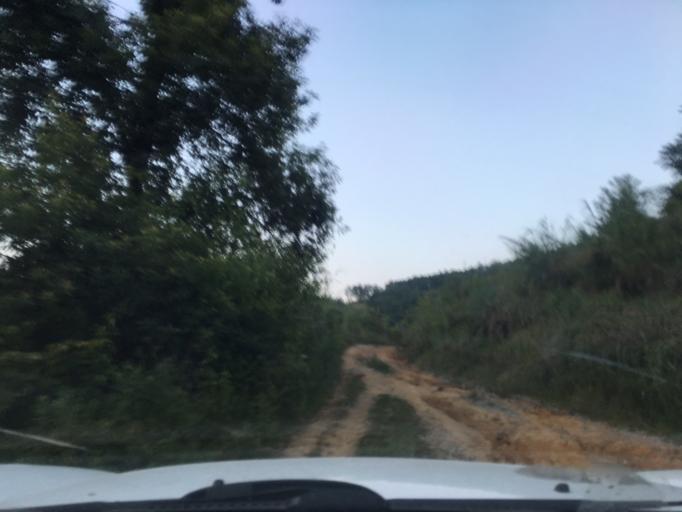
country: CN
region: Guangxi Zhuangzu Zizhiqu
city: Xinzhou
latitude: 25.3501
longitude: 105.7397
